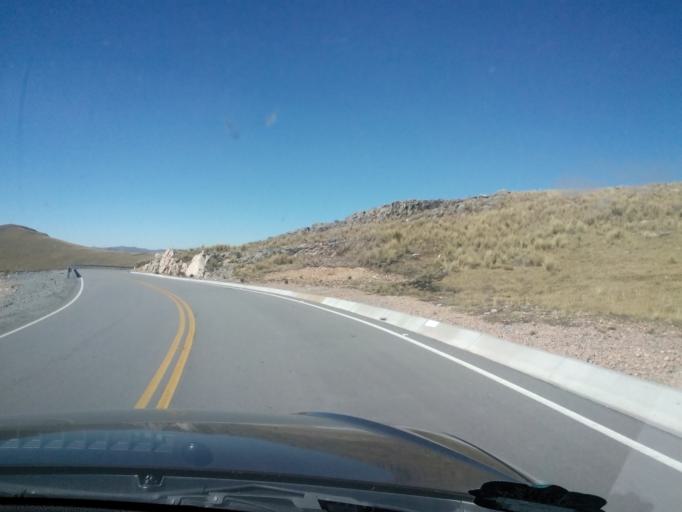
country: PE
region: Ayacucho
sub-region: Provincia de Huamanga
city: Acocro
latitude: -13.3728
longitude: -74.0801
